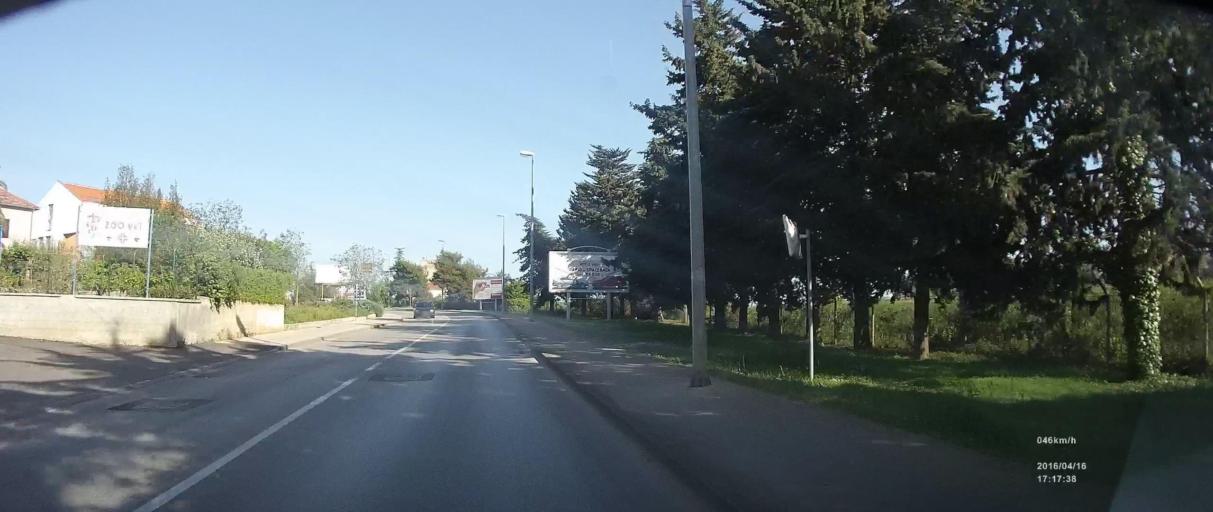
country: HR
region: Zadarska
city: Zadar
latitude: 44.1023
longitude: 15.2485
